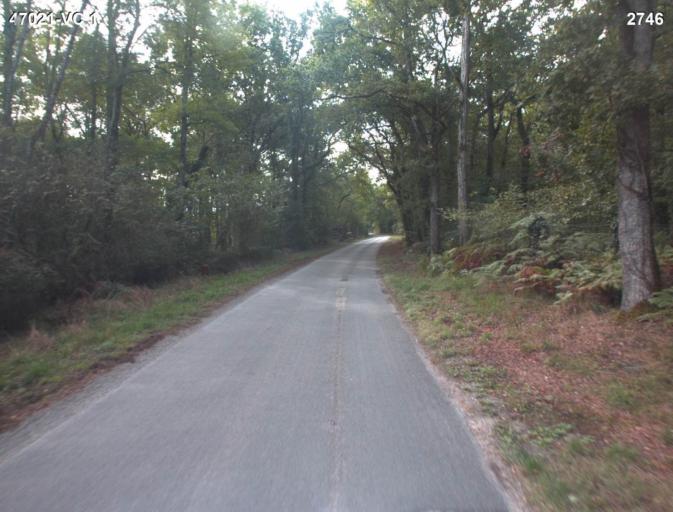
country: FR
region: Aquitaine
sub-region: Departement du Lot-et-Garonne
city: Barbaste
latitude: 44.1433
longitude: 0.2949
